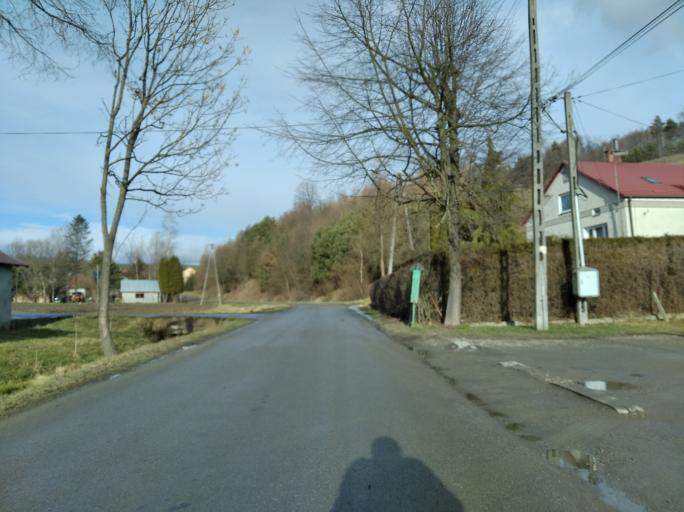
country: PL
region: Subcarpathian Voivodeship
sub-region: Powiat strzyzowski
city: Strzyzow
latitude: 49.8961
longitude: 21.7546
